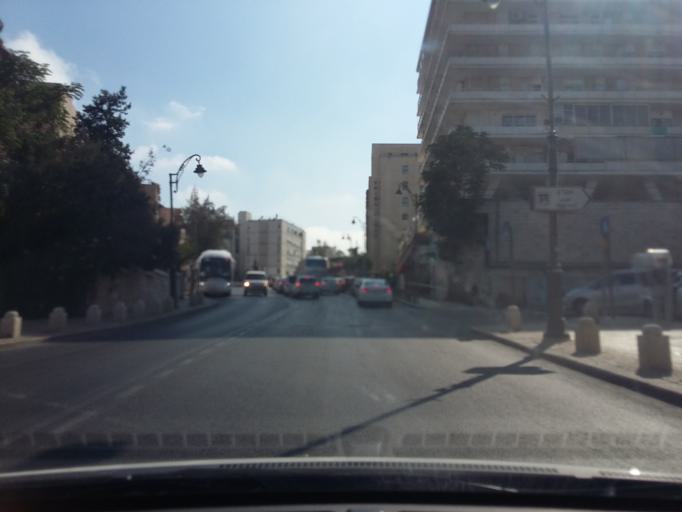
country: IL
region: Jerusalem
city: West Jerusalem
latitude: 31.7760
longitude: 35.2187
